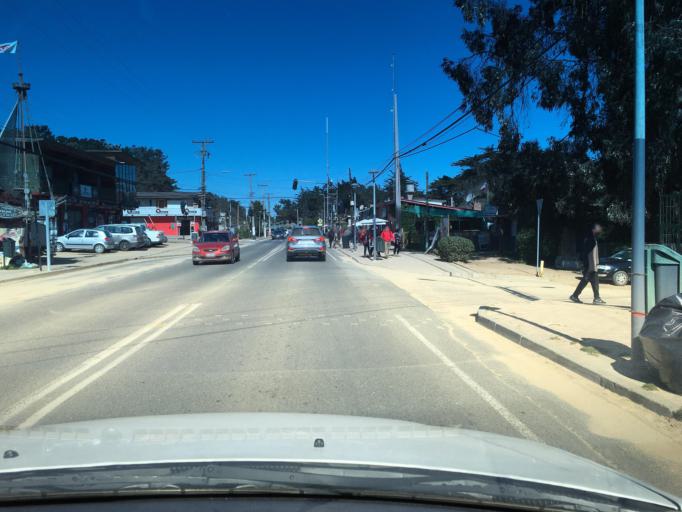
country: CL
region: Valparaiso
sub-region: San Antonio Province
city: El Tabo
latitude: -33.4407
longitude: -71.6832
